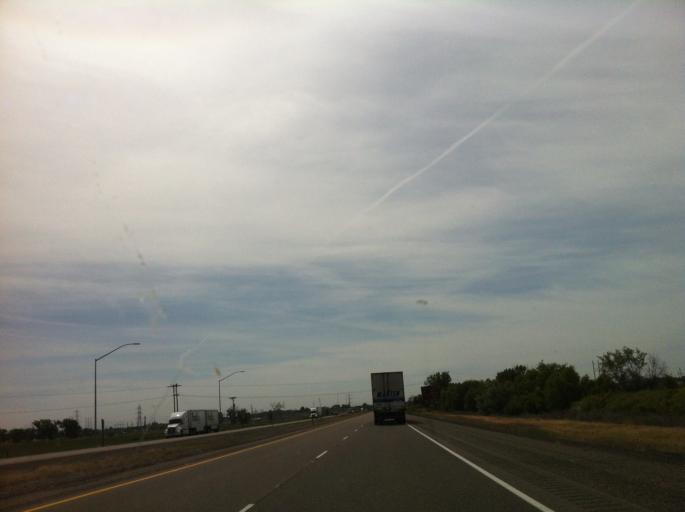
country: US
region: Oregon
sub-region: Malheur County
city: Ontario
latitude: 44.0587
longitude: -116.9894
